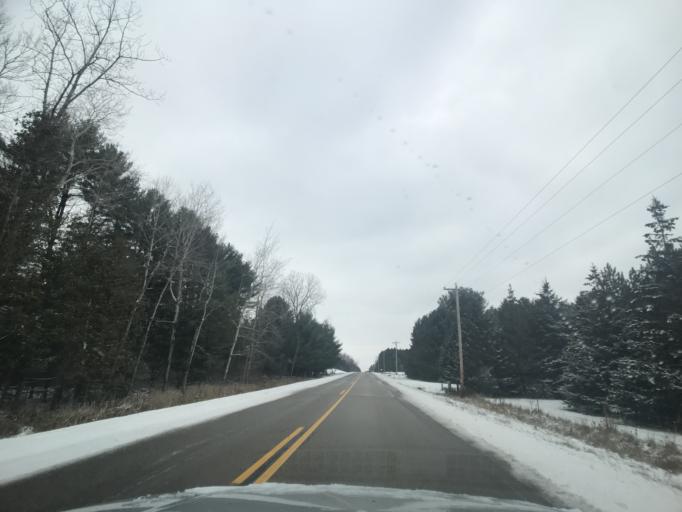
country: US
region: Wisconsin
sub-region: Brown County
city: Suamico
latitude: 44.7062
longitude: -88.0898
